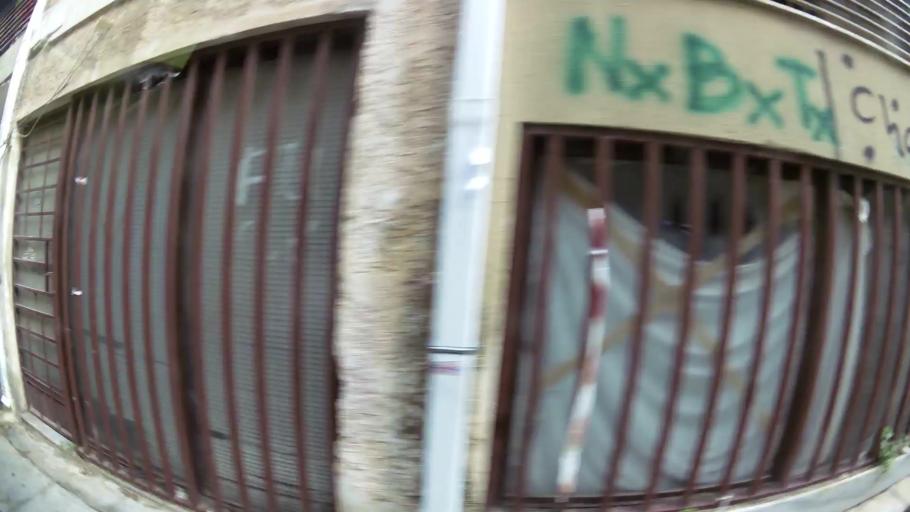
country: GR
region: Attica
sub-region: Nomarchia Athinas
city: Kaisariani
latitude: 37.9776
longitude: 23.7662
